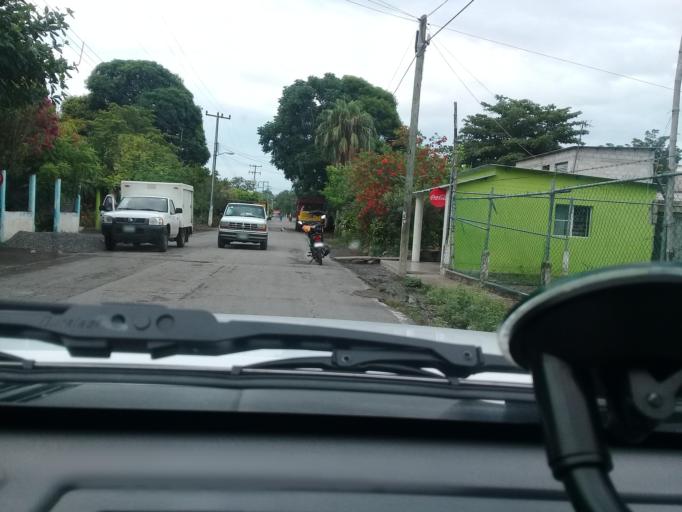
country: MX
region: Veracruz
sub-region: Paso de Ovejas
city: El Hatito
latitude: 19.3163
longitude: -96.3824
